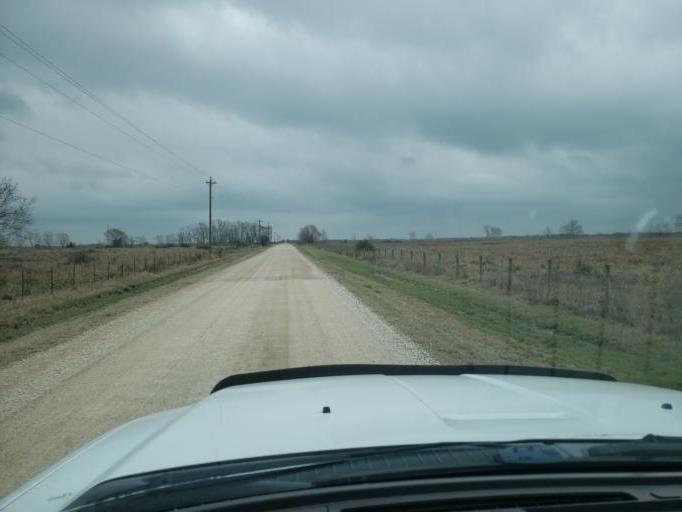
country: US
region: Texas
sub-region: Fort Bend County
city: Needville
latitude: 29.3624
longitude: -95.7365
